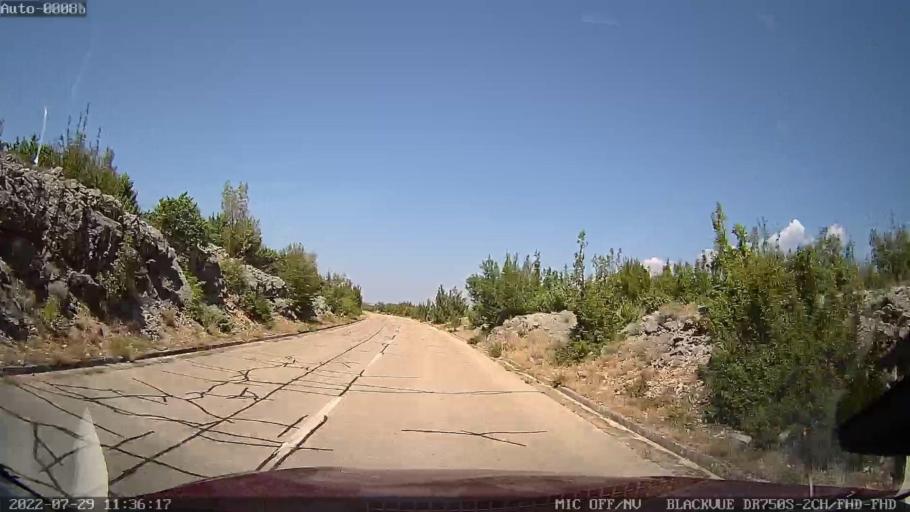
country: HR
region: Zadarska
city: Obrovac
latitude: 44.1886
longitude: 15.7007
